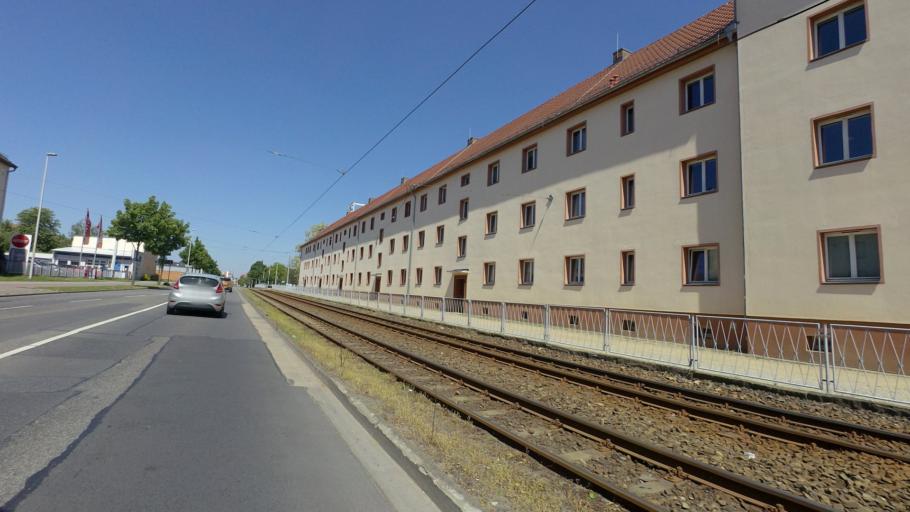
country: DE
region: Brandenburg
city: Cottbus
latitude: 51.7387
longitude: 14.3352
